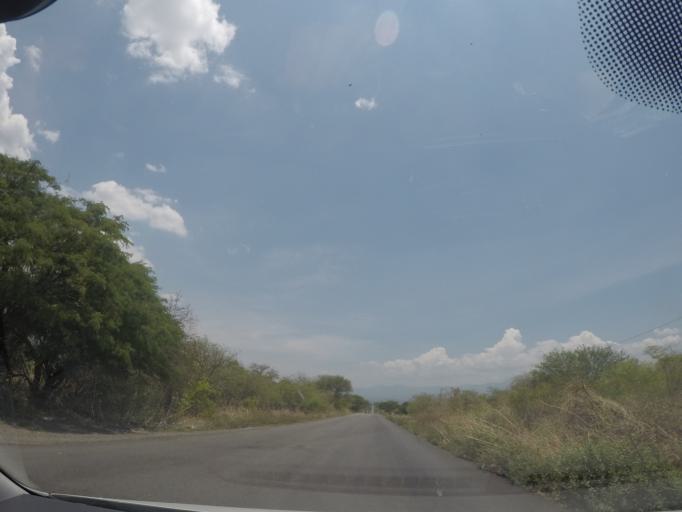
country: MX
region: Oaxaca
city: Santa Maria Jalapa del Marques
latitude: 16.4397
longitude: -95.4745
